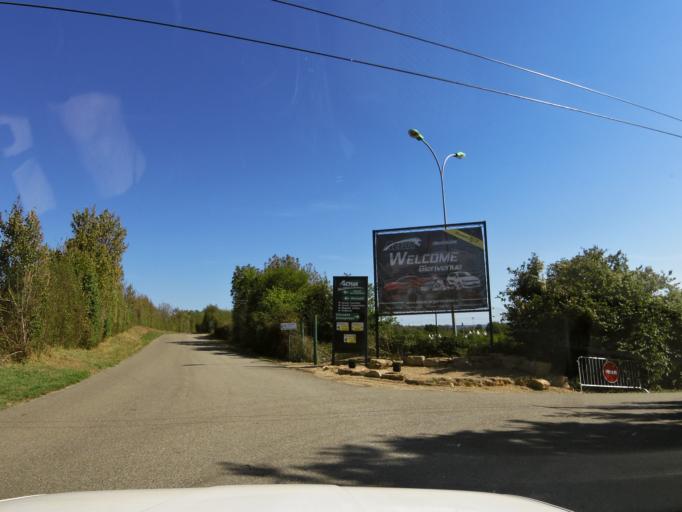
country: FR
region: Rhone-Alpes
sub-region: Departement de l'Isere
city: Grenay
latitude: 45.6860
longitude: 5.0741
